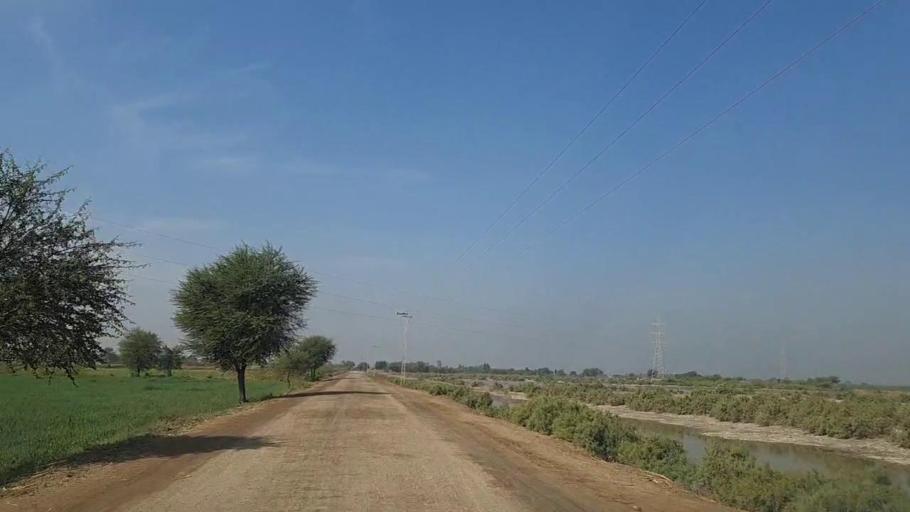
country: PK
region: Sindh
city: Mirpur Khas
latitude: 25.4825
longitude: 68.9790
